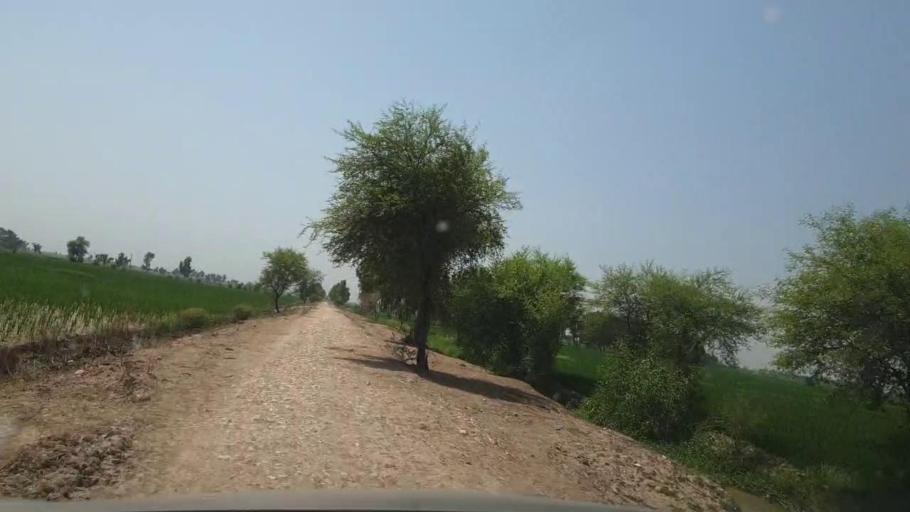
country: PK
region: Sindh
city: Warah
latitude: 27.5117
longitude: 67.7717
